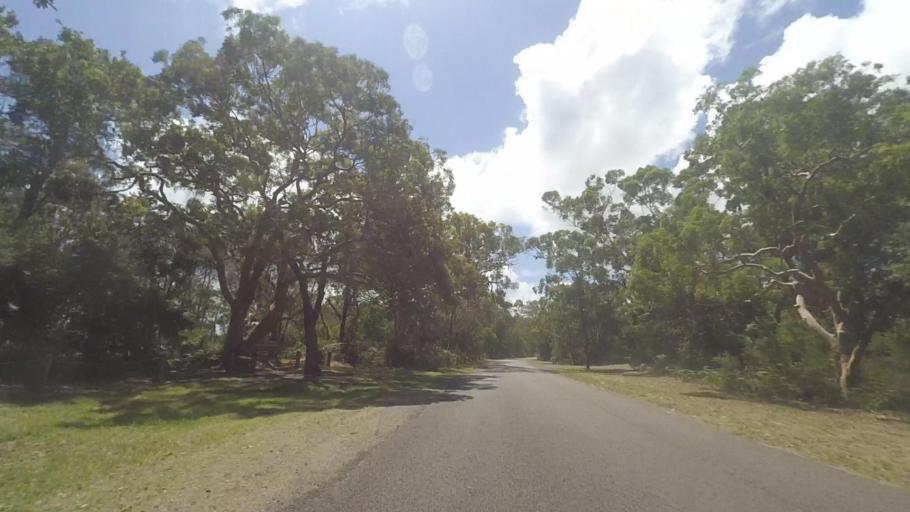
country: AU
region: New South Wales
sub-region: Great Lakes
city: Bulahdelah
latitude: -32.5096
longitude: 152.3186
